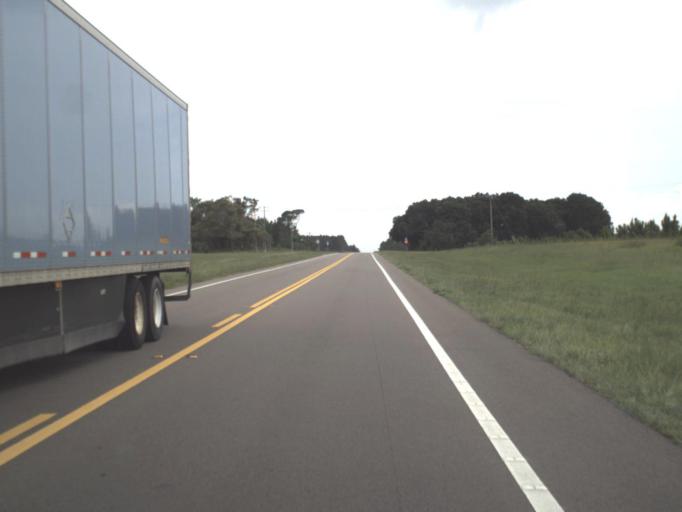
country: US
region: Florida
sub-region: Pasco County
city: Zephyrhills North
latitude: 28.3092
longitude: -82.1651
